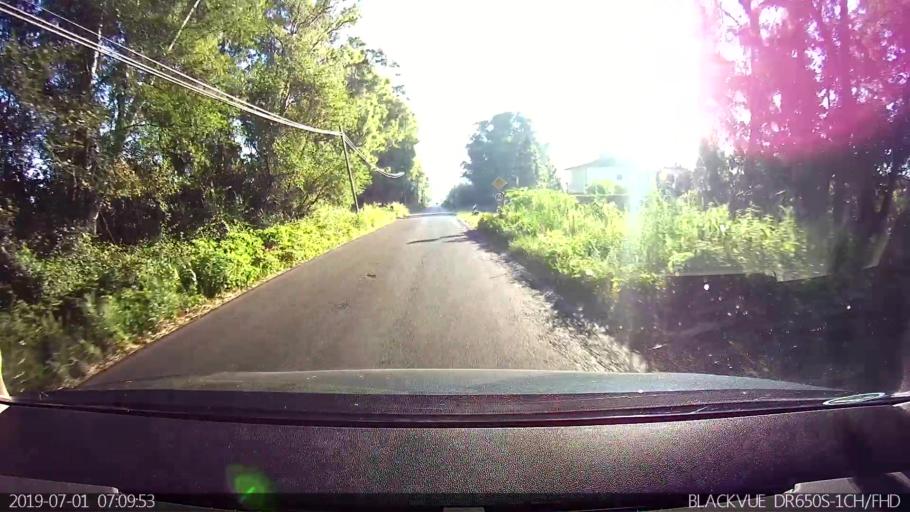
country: IT
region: Latium
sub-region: Provincia di Latina
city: Borgo Hermada
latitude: 41.3081
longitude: 13.1648
